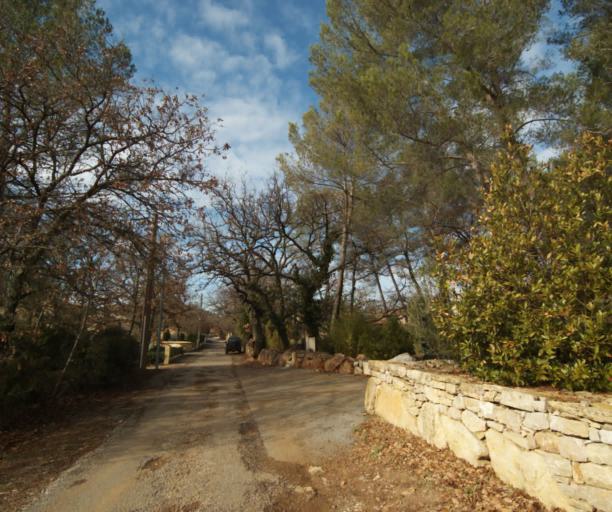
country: FR
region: Provence-Alpes-Cote d'Azur
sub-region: Departement du Var
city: Trans-en-Provence
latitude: 43.5205
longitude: 6.5060
